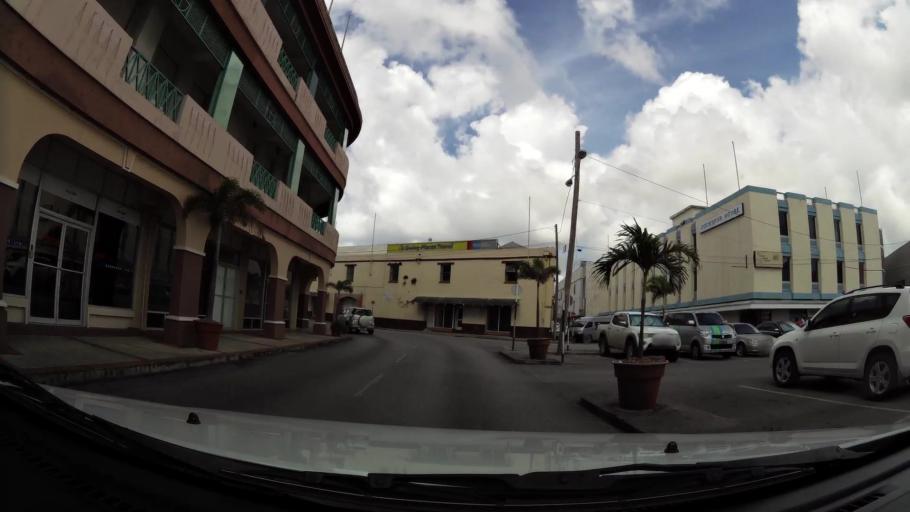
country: BB
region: Saint Michael
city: Bridgetown
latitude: 13.0964
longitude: -59.6172
